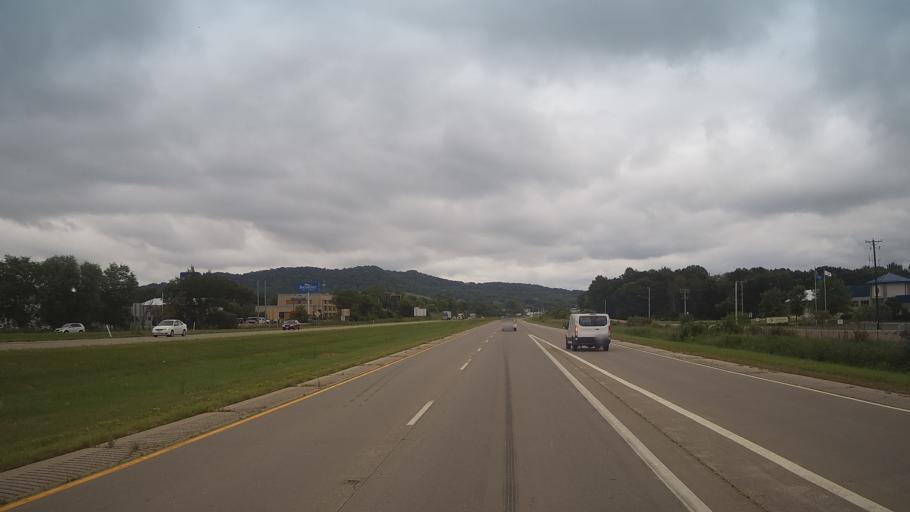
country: US
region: Wisconsin
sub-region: La Crosse County
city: Onalaska
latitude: 43.8764
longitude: -91.1793
